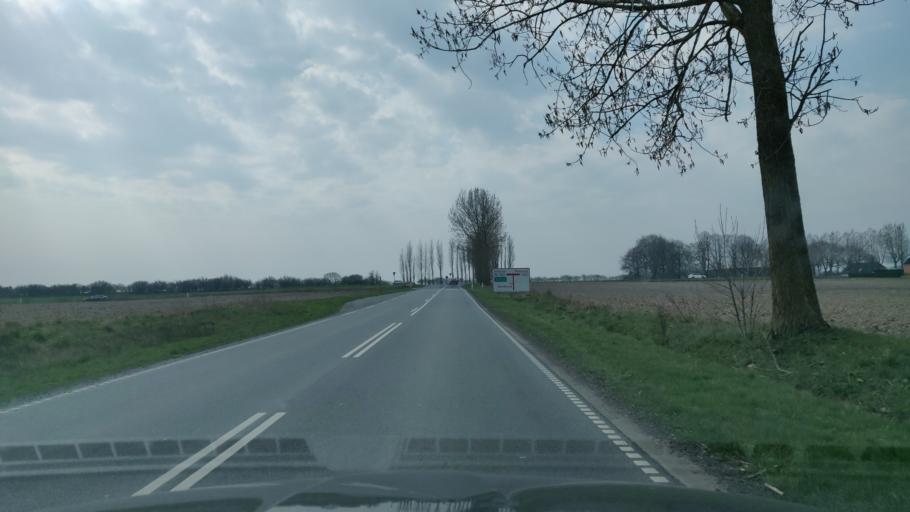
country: DK
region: South Denmark
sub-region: Nordfyns Kommune
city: Sonderso
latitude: 55.4923
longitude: 10.2376
